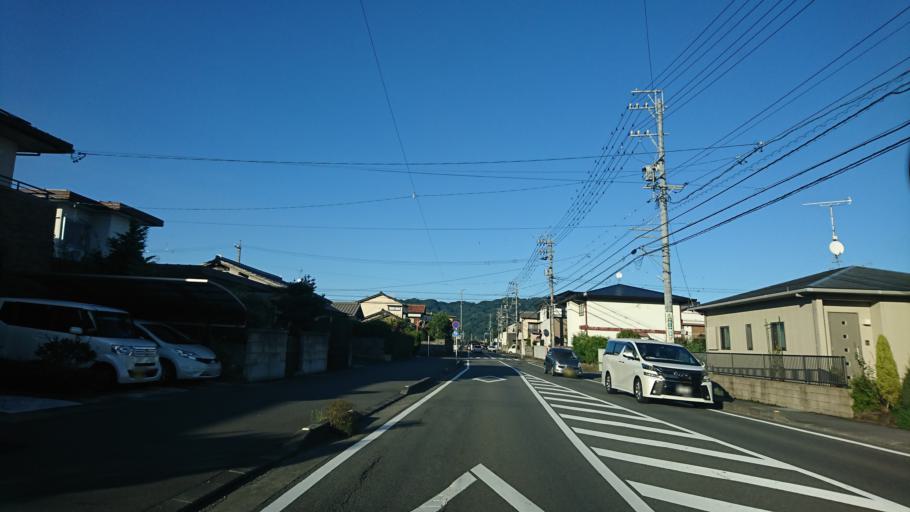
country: JP
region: Shizuoka
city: Fujieda
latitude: 34.8703
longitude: 138.2787
